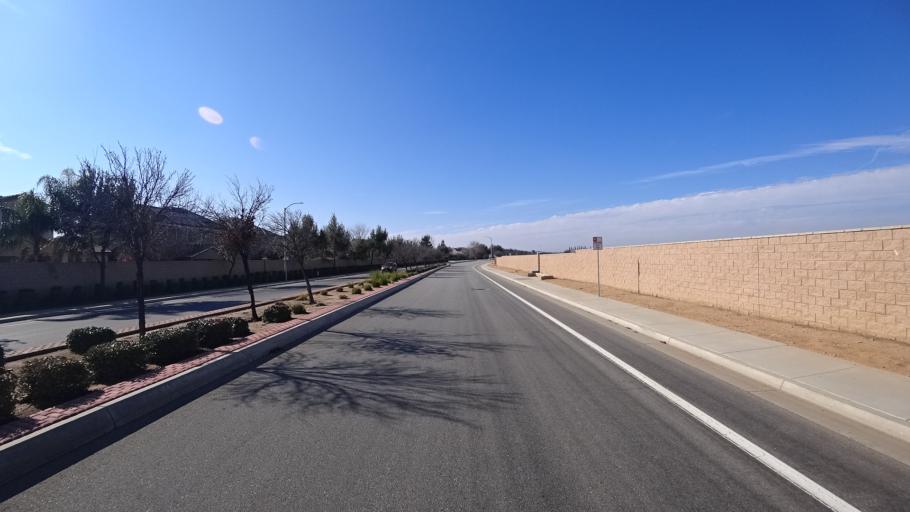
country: US
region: California
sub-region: Kern County
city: Oildale
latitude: 35.4096
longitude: -118.8807
